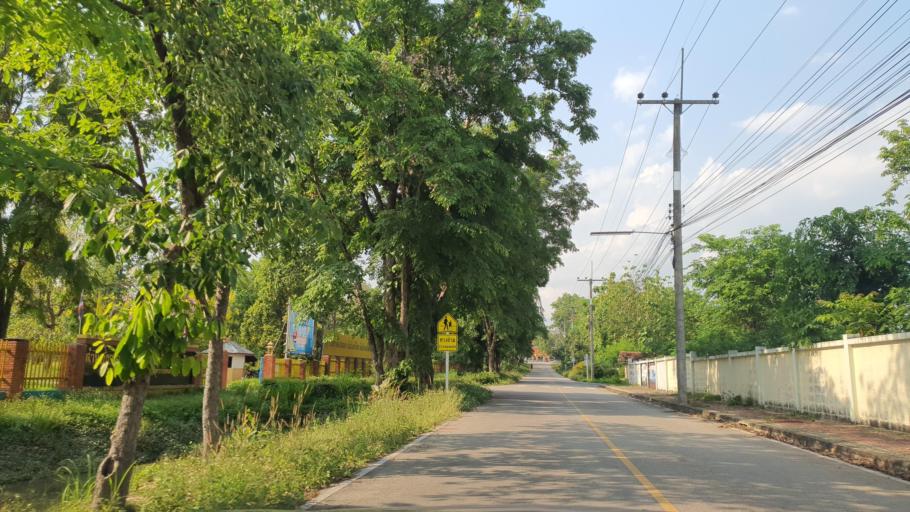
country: TH
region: Chiang Mai
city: San Pa Tong
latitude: 18.6468
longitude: 98.8477
